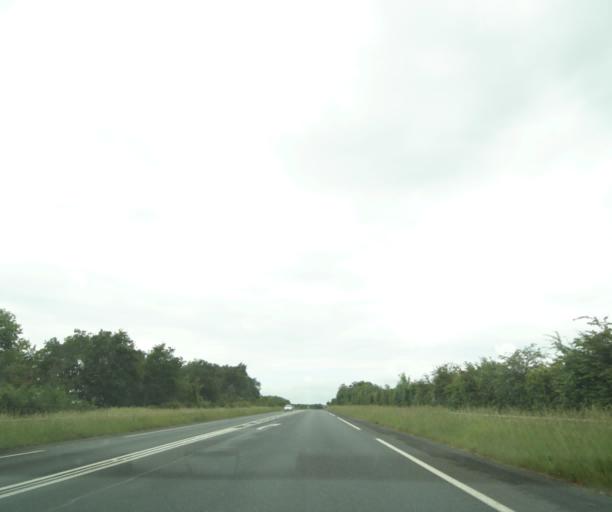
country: FR
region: Poitou-Charentes
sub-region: Departement des Deux-Sevres
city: Saint-Varent
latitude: 46.8559
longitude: -0.2088
